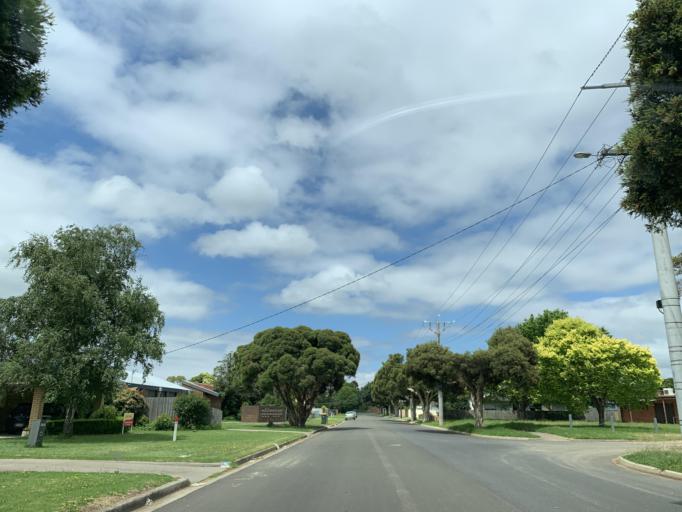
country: AU
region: Victoria
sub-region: Wellington
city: Sale
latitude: -38.1046
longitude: 147.0865
